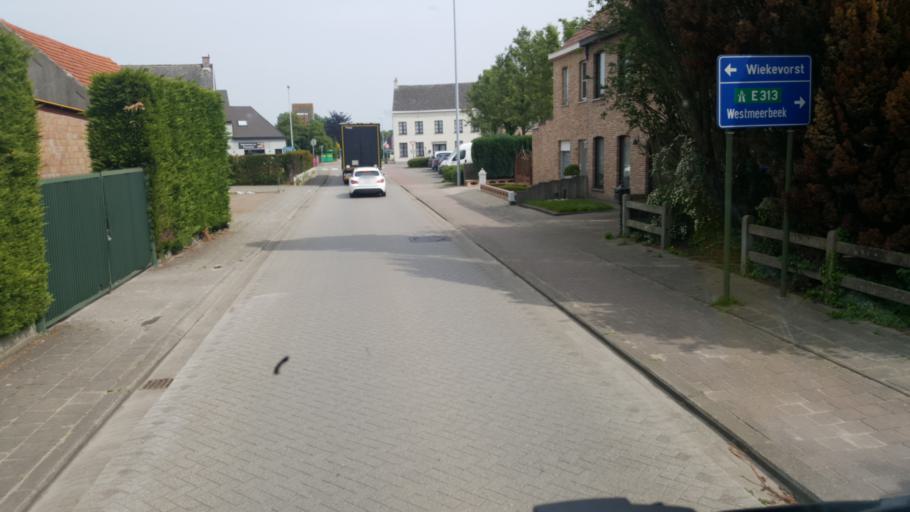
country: BE
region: Flanders
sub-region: Provincie Antwerpen
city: Hulshout
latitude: 51.0908
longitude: 4.8394
